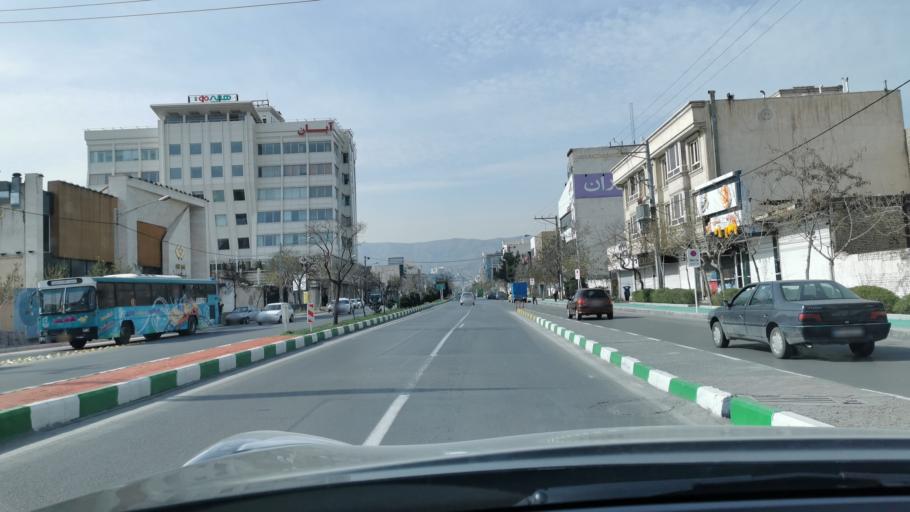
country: IR
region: Razavi Khorasan
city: Mashhad
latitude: 36.3216
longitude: 59.5141
